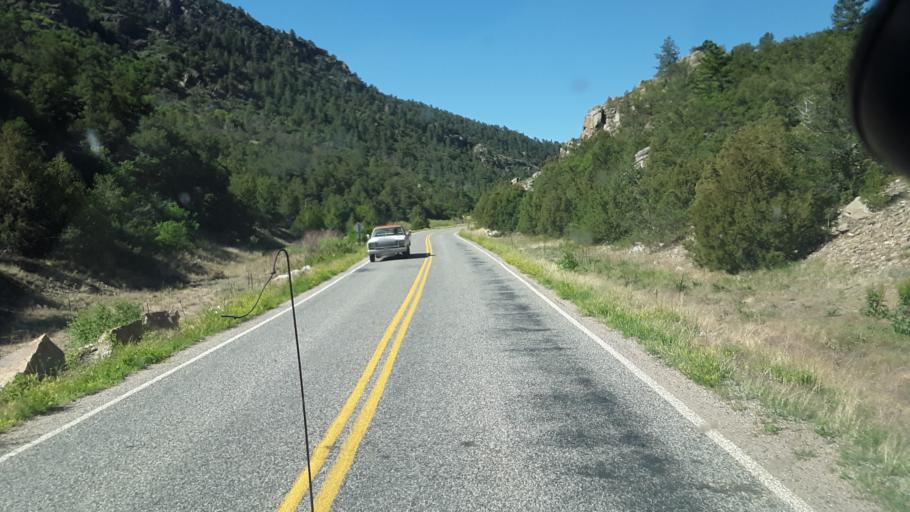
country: US
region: Colorado
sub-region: Fremont County
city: Canon City
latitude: 38.3972
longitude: -105.4464
